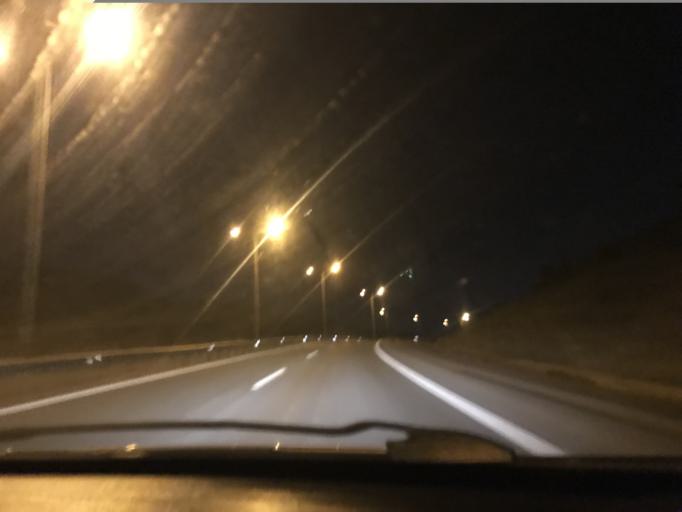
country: TR
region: Ankara
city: Etimesgut
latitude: 39.8652
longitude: 32.6265
